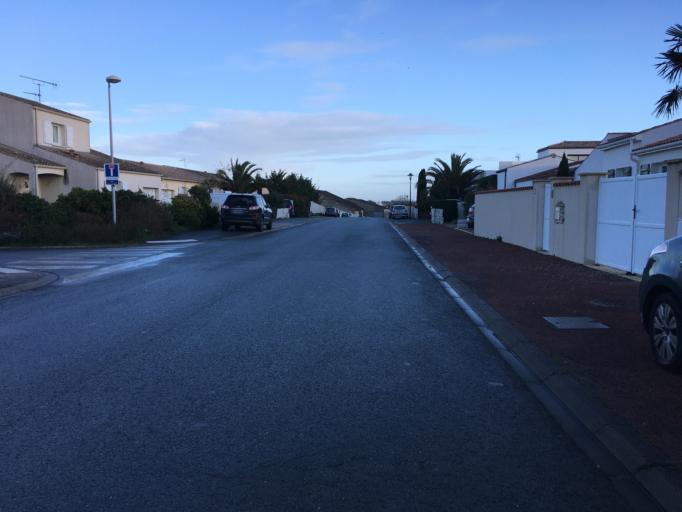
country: FR
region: Poitou-Charentes
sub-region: Departement de la Charente-Maritime
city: Nieul-sur-Mer
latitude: 46.2011
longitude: -1.1661
